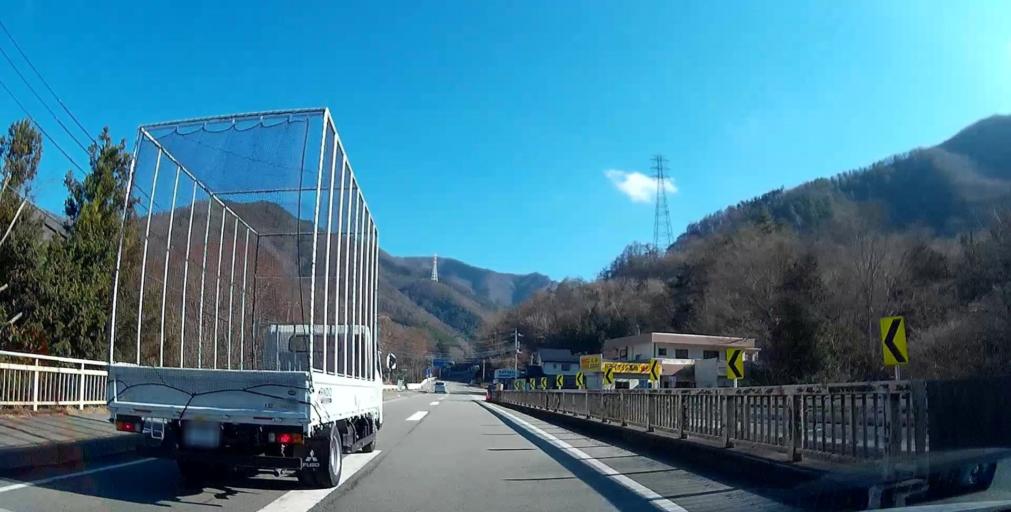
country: JP
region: Yamanashi
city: Fujikawaguchiko
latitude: 35.5753
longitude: 138.7643
